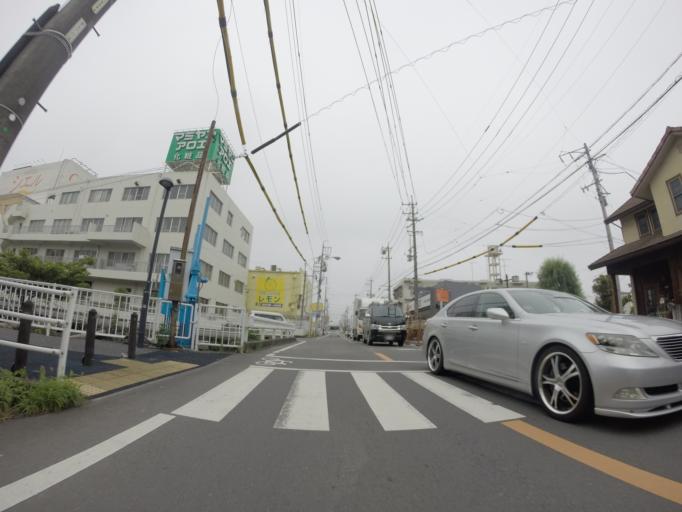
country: JP
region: Shizuoka
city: Shizuoka-shi
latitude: 34.9489
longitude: 138.3979
